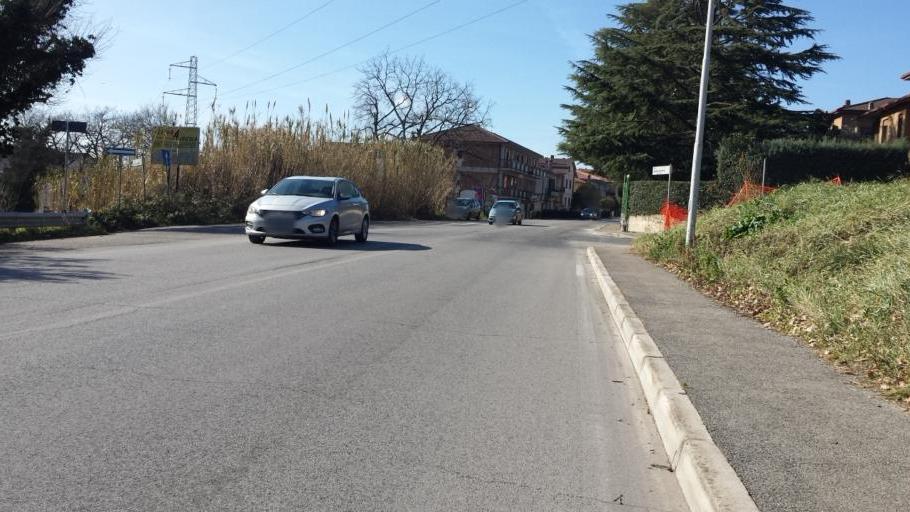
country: IT
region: Umbria
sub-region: Provincia di Terni
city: Terni
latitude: 42.5911
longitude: 12.5944
